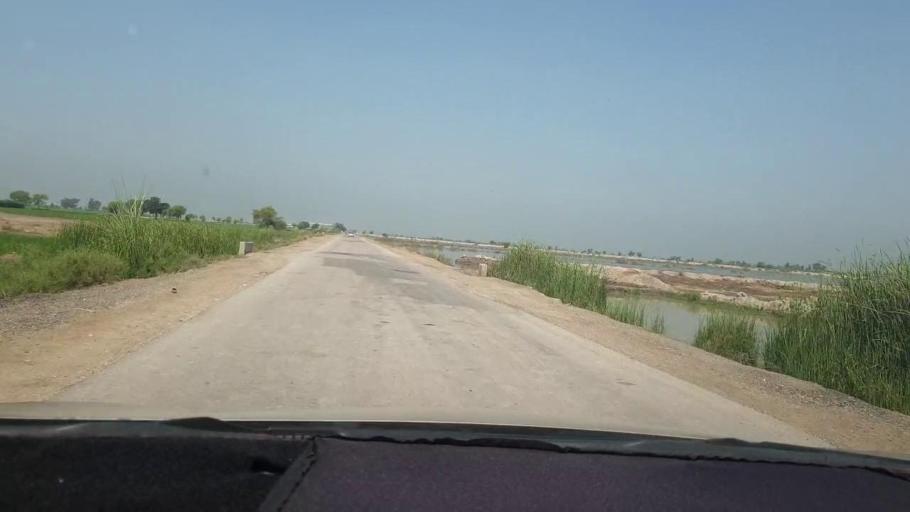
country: PK
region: Sindh
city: Shahdadkot
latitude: 27.8421
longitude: 68.0054
